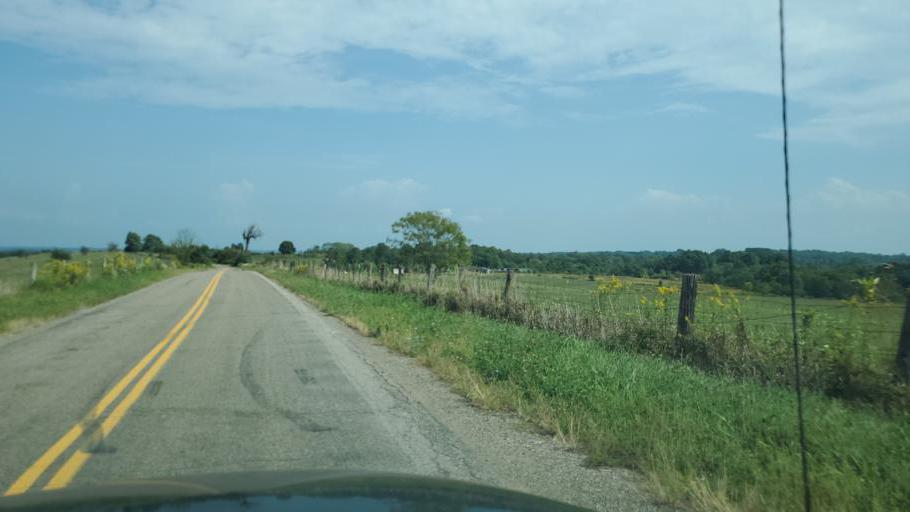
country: US
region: Ohio
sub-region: Muskingum County
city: Zanesville
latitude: 39.9374
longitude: -82.0897
